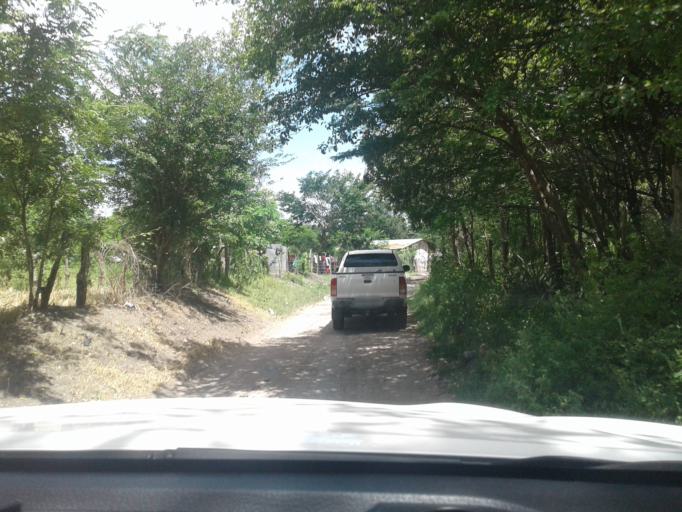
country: NI
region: Matagalpa
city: Terrabona
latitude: 12.5699
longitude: -86.0377
